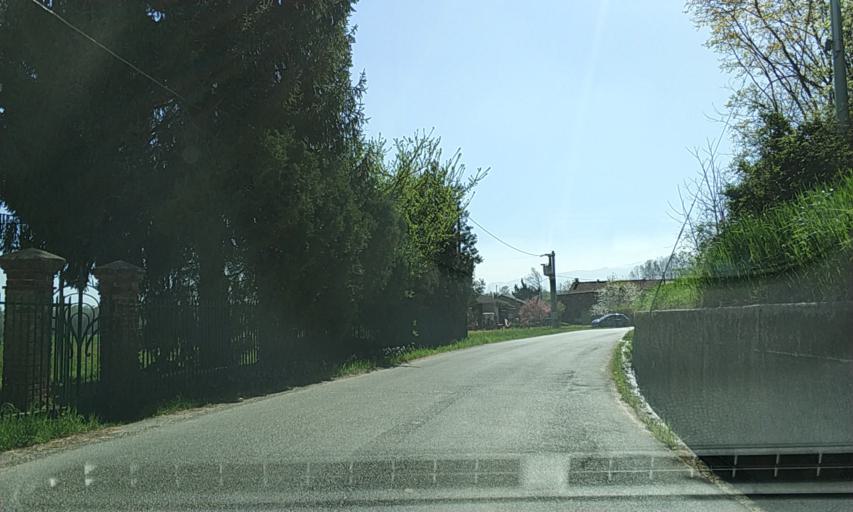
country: IT
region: Piedmont
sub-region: Provincia di Torino
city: Rivara
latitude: 45.3185
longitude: 7.6426
